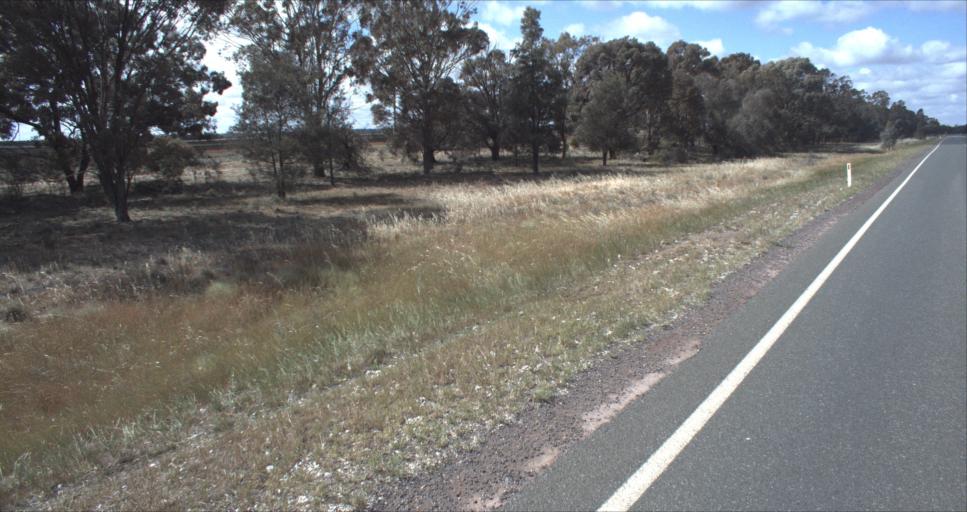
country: AU
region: New South Wales
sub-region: Murrumbidgee Shire
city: Darlington Point
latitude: -34.5872
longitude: 146.1641
